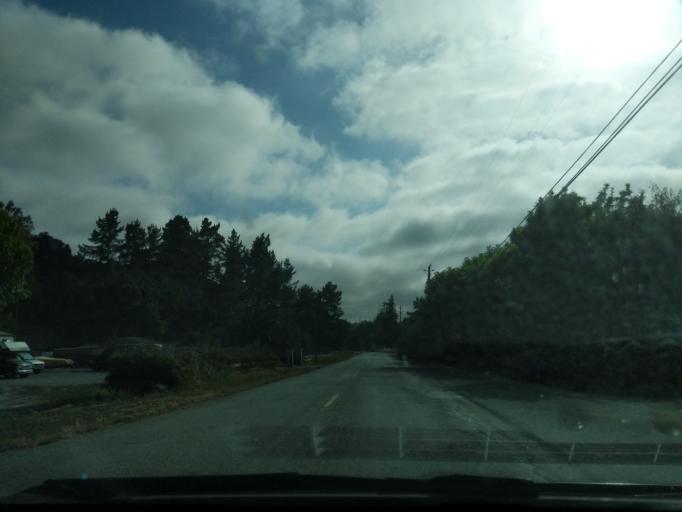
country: US
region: California
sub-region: Monterey County
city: Prunedale
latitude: 36.7967
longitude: -121.6534
